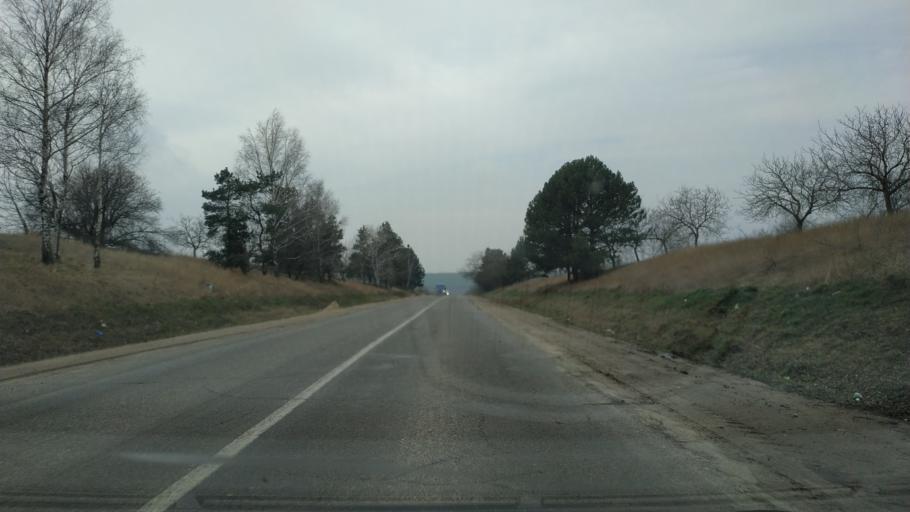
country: MD
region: Cahul
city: Cahul
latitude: 45.9466
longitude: 28.3106
